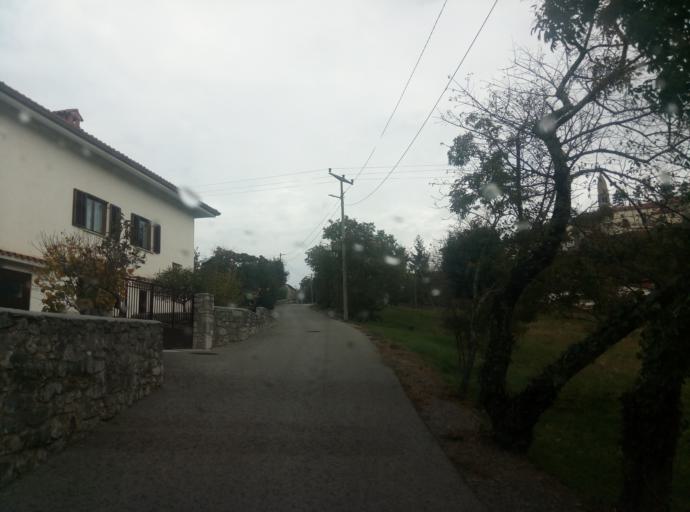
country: SI
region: Ajdovscina
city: Lokavec
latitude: 45.8215
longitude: 13.8451
